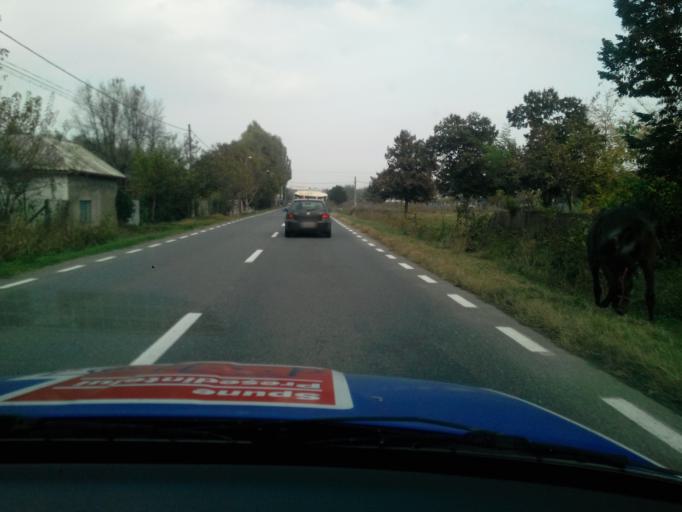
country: RO
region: Tulcea
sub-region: Comuna Somova
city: Somova
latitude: 45.1896
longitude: 28.6564
